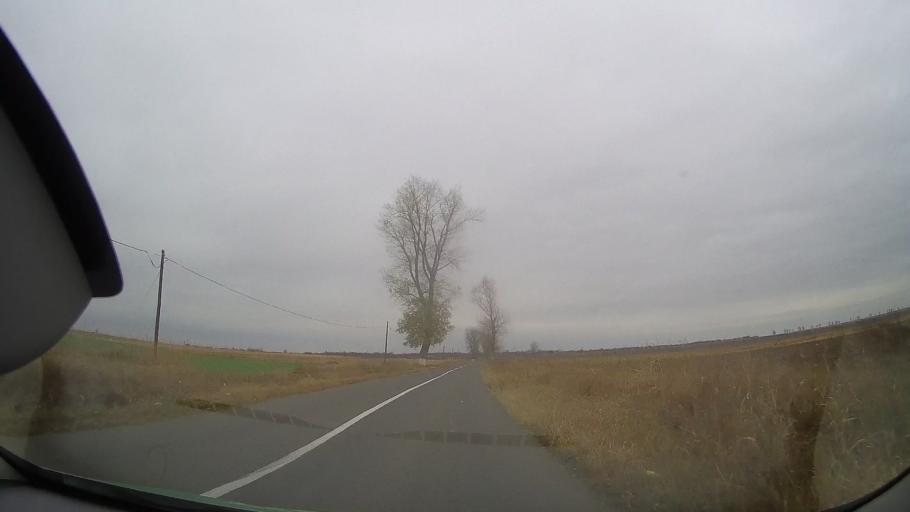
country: RO
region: Braila
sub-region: Comuna Budesti
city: Tataru
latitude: 44.8362
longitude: 27.4156
